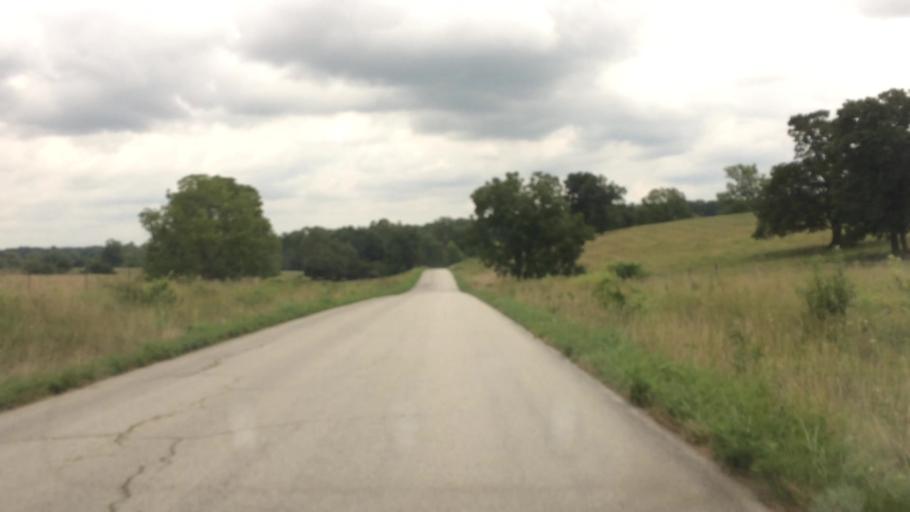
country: US
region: Missouri
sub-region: Greene County
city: Strafford
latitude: 37.3053
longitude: -93.0743
